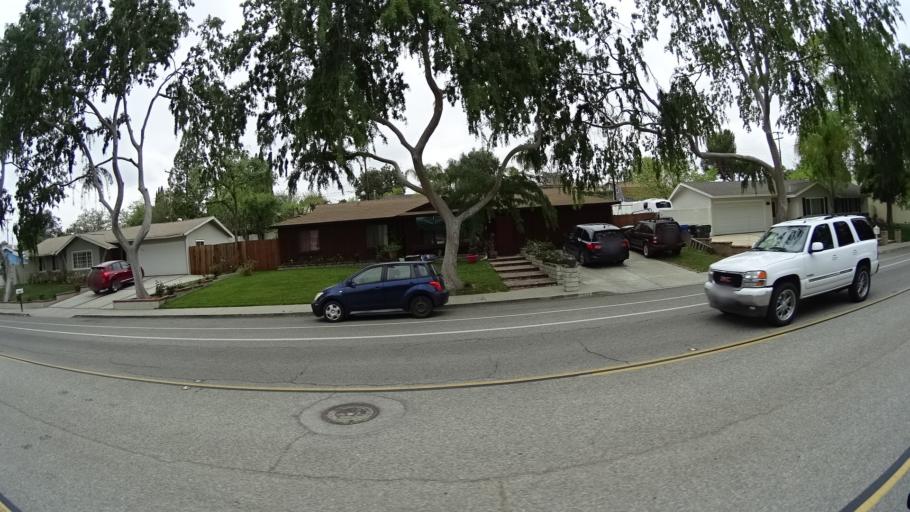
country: US
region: California
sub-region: Ventura County
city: Thousand Oaks
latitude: 34.2113
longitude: -118.8589
